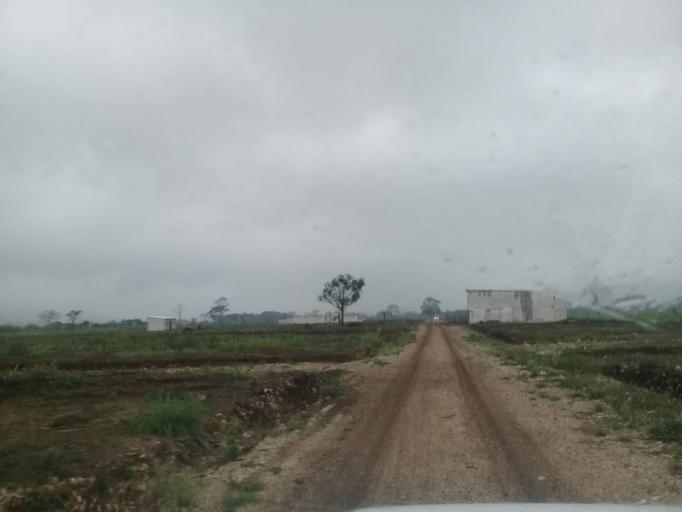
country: MX
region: Veracruz
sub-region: Cordoba
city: Veinte de Noviembre
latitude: 18.8601
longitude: -96.9600
